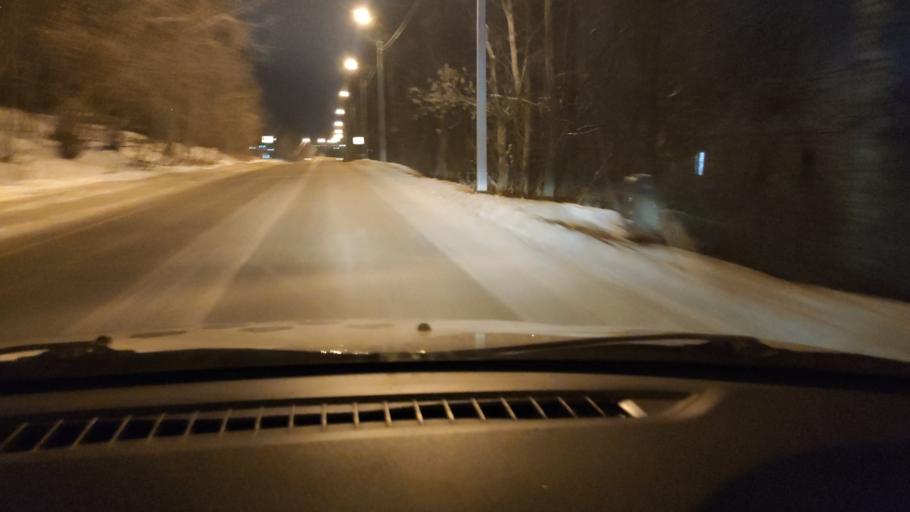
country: RU
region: Perm
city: Perm
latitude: 58.1000
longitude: 56.3051
